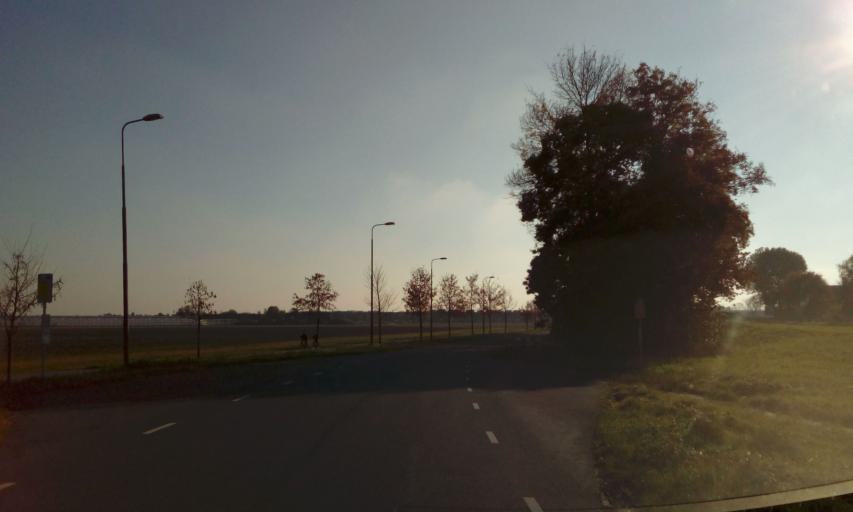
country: NL
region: South Holland
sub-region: Gemeente Lansingerland
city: Bleiswijk
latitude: 52.0239
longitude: 4.5801
